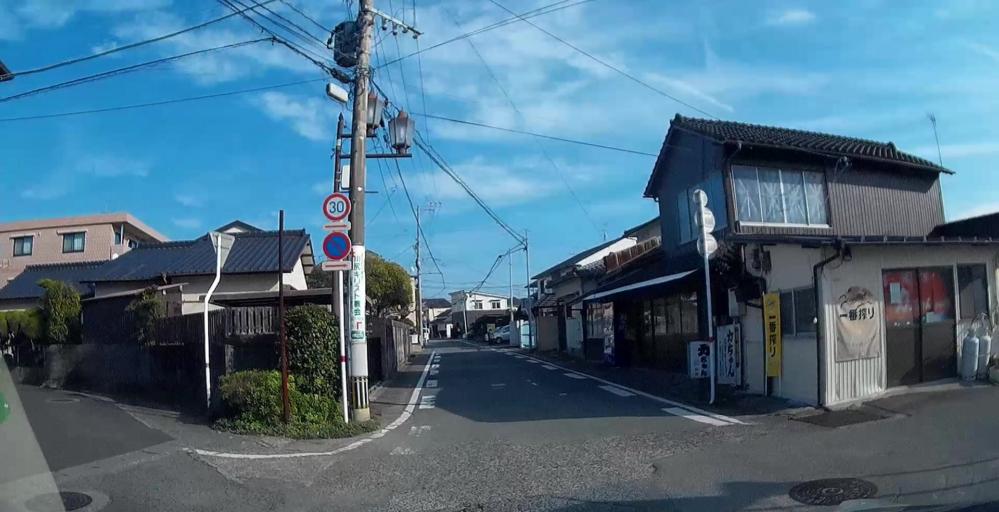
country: JP
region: Kumamoto
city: Uto
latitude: 32.7437
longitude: 130.6804
